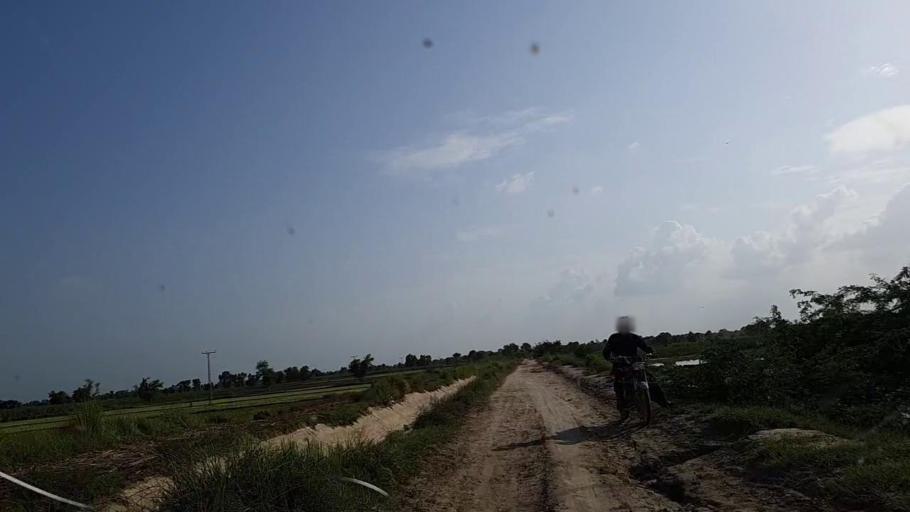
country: PK
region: Sindh
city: Bhiria
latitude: 26.8669
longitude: 68.2557
